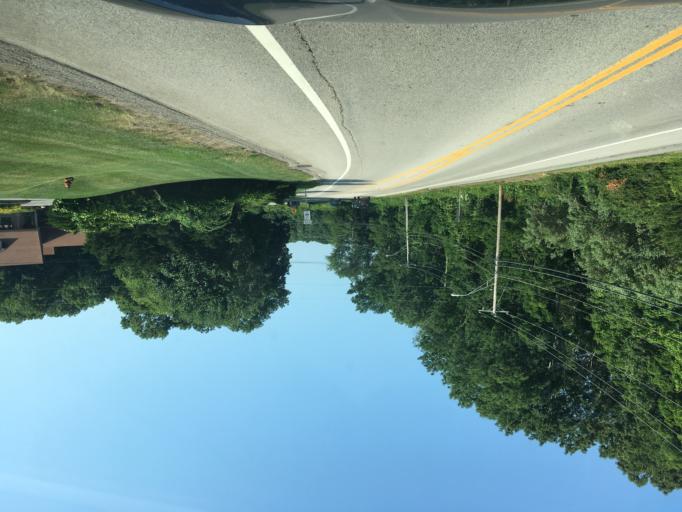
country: US
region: Rhode Island
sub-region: Washington County
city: Exeter
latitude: 41.5855
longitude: -71.5017
